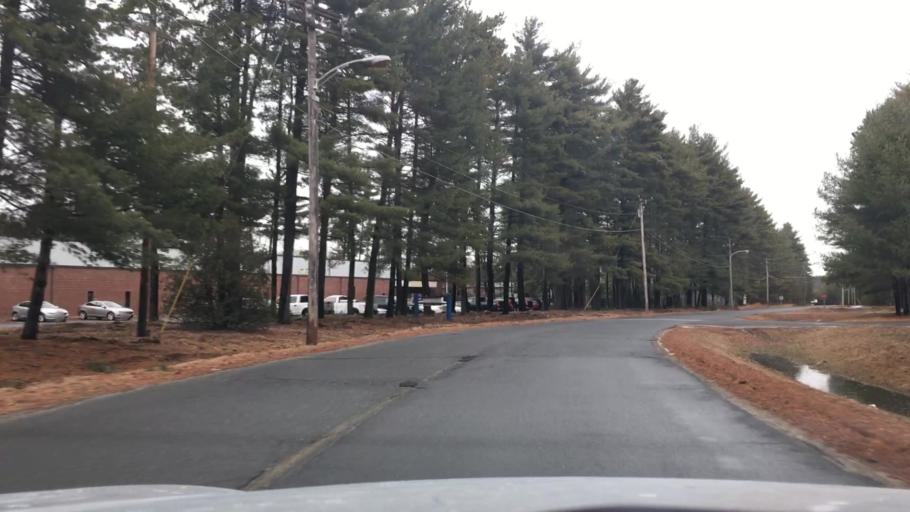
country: US
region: Massachusetts
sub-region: Franklin County
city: Orange
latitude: 42.5631
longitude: -72.2864
